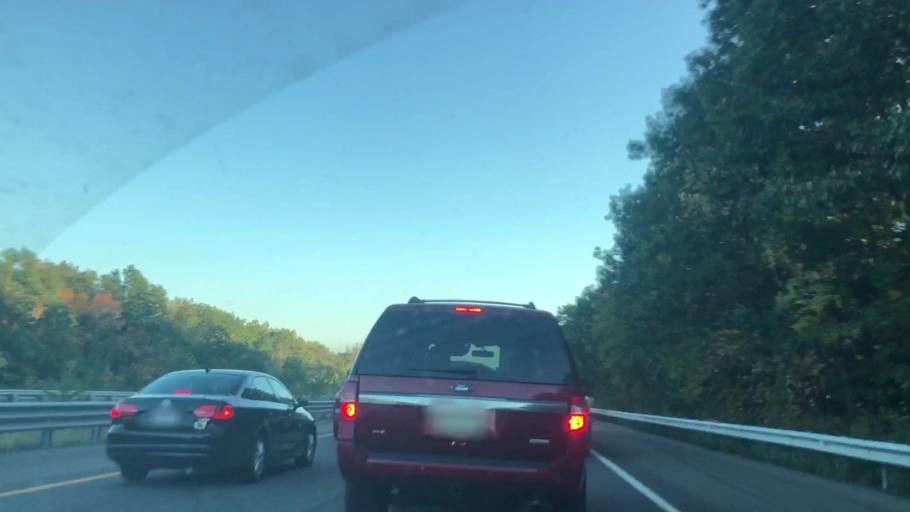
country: US
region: Massachusetts
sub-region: Franklin County
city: South Deerfield
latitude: 42.5261
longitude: -72.6271
